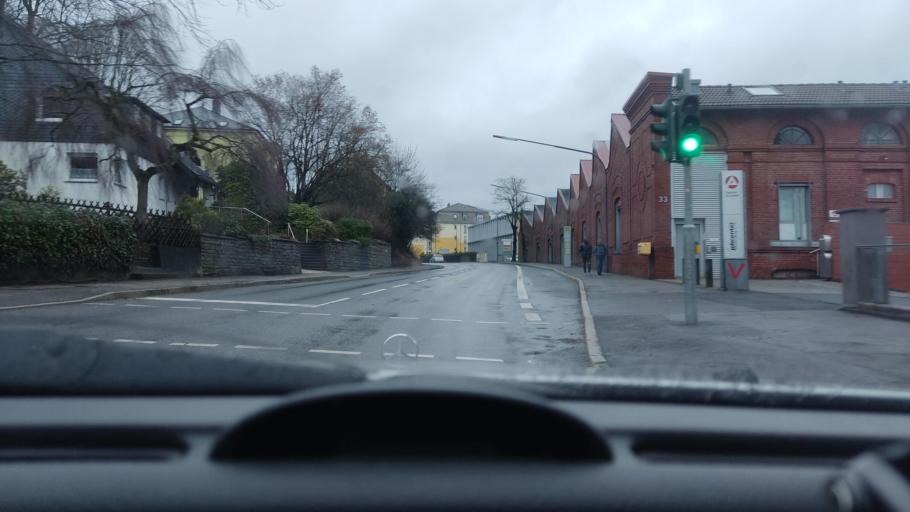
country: DE
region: North Rhine-Westphalia
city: Wermelskirchen
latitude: 51.1351
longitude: 7.2128
